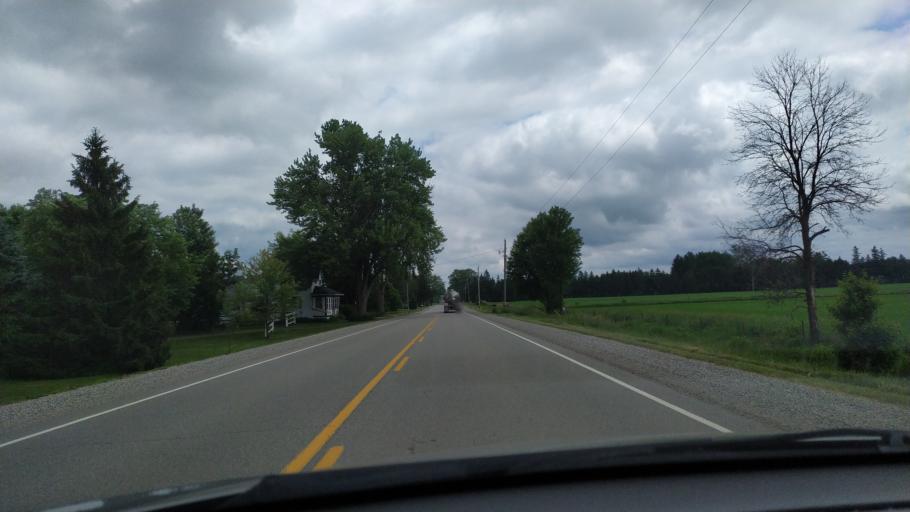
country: CA
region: Ontario
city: Stratford
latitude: 43.4250
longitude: -80.8276
